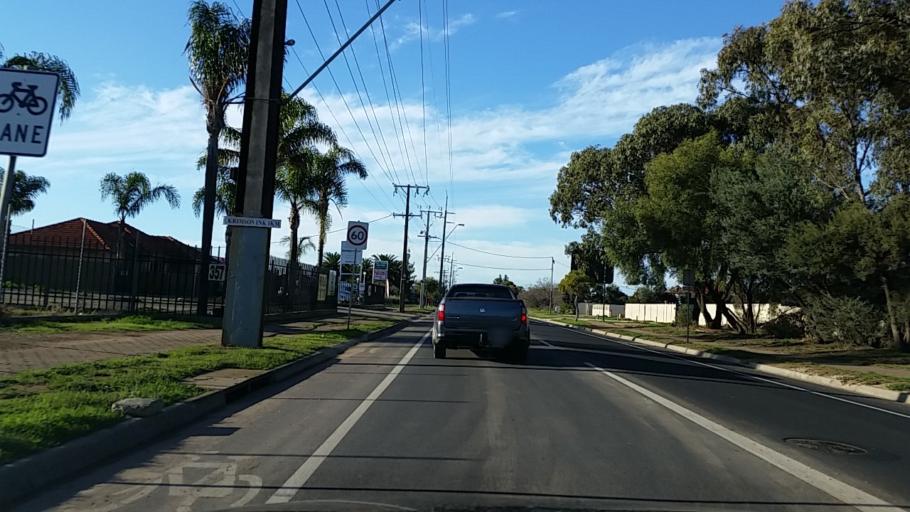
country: AU
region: South Australia
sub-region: Salisbury
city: Salisbury
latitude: -34.7899
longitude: 138.6009
